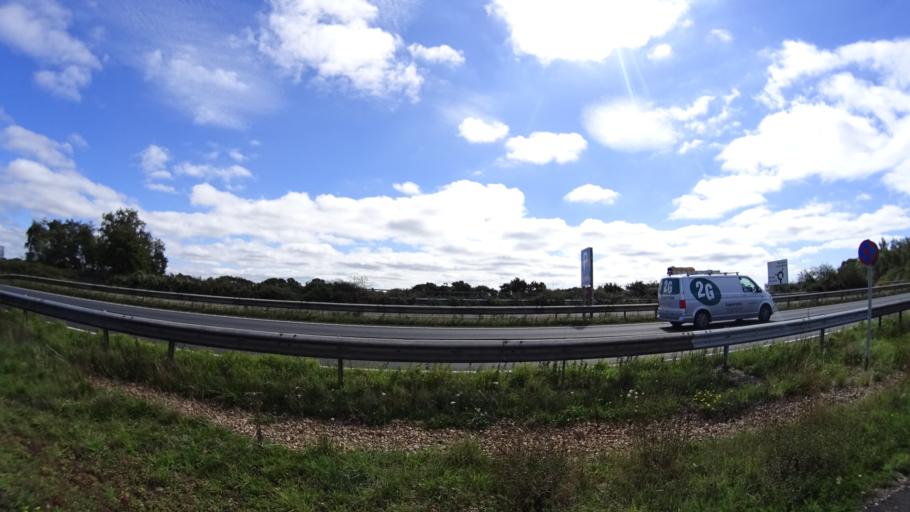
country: GB
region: England
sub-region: Hampshire
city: Ringwood
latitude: 50.8554
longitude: -1.7280
